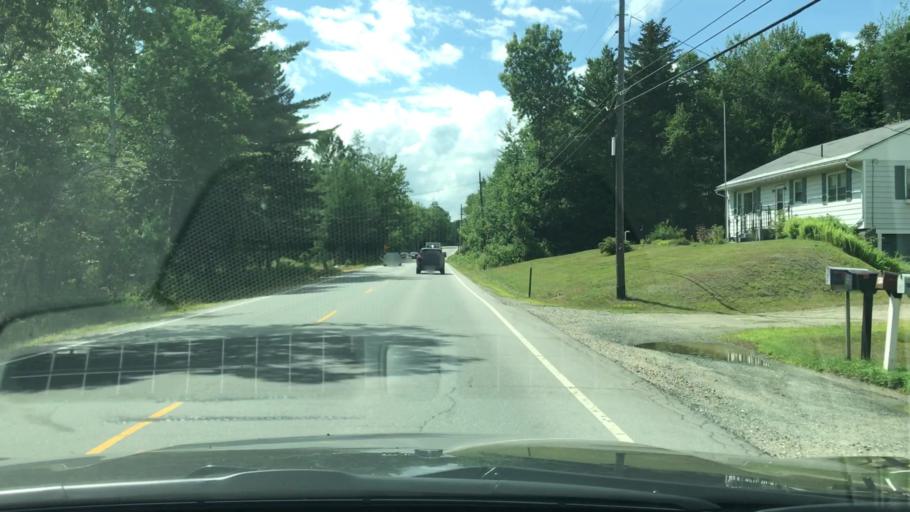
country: US
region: New Hampshire
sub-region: Coos County
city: Jefferson
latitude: 44.3601
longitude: -71.3717
